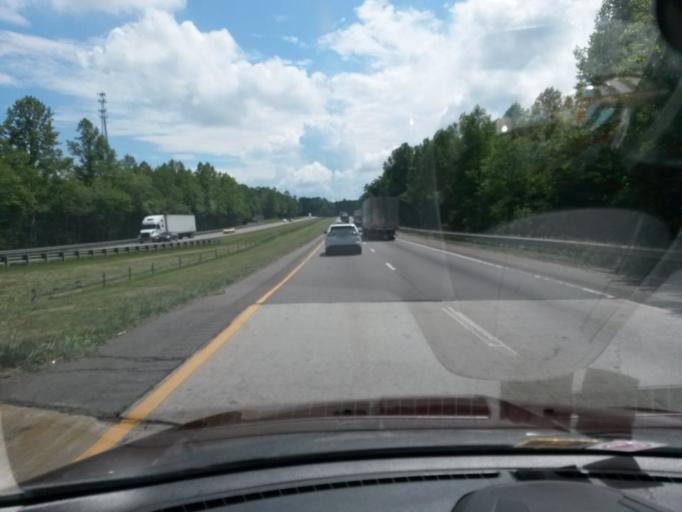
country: US
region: North Carolina
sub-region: Surry County
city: Dobson
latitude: 36.4457
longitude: -80.7754
